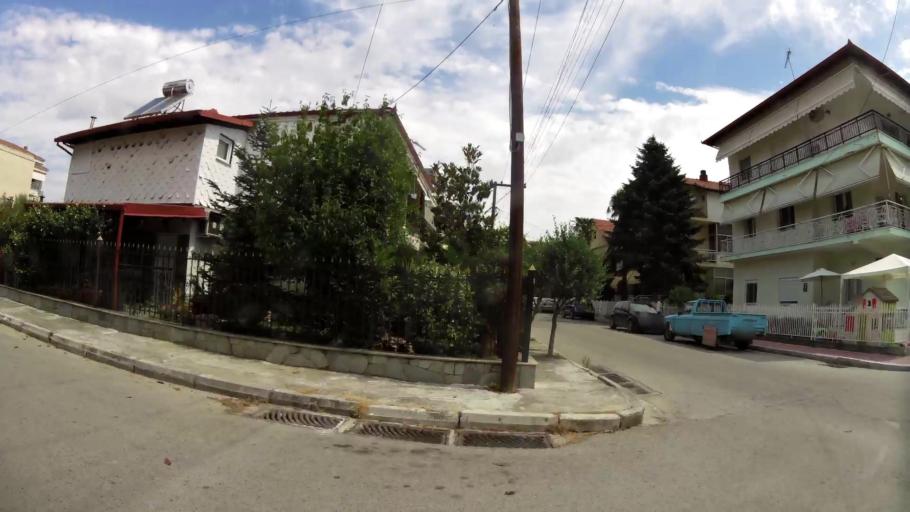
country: GR
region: Central Macedonia
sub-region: Nomos Pierias
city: Katerini
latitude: 40.2780
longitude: 22.4995
